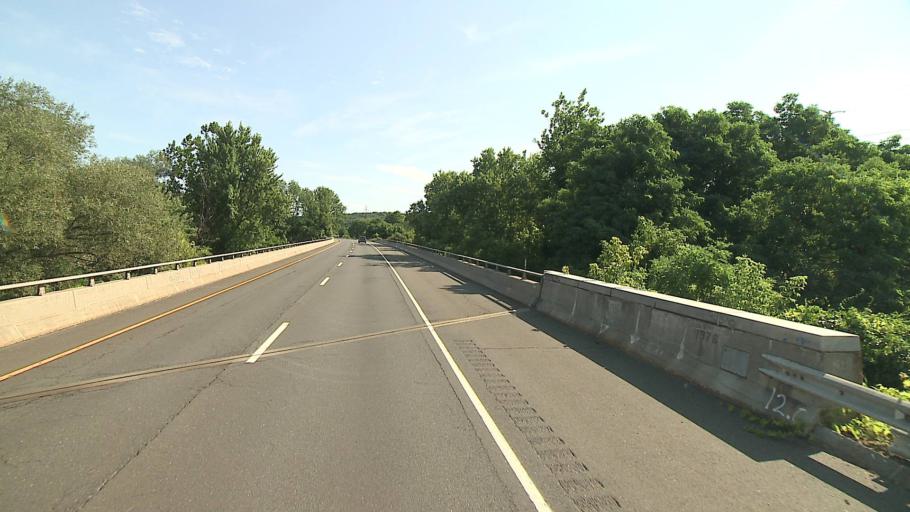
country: US
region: Connecticut
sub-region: Fairfield County
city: Bethel
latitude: 41.4391
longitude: -73.3999
